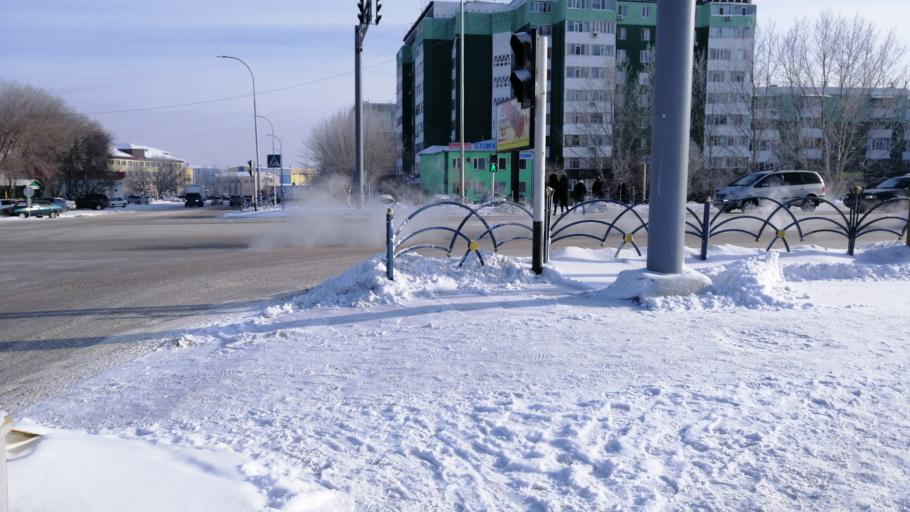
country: KZ
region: Aqtoebe
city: Aqtobe
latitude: 50.2897
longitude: 57.1961
